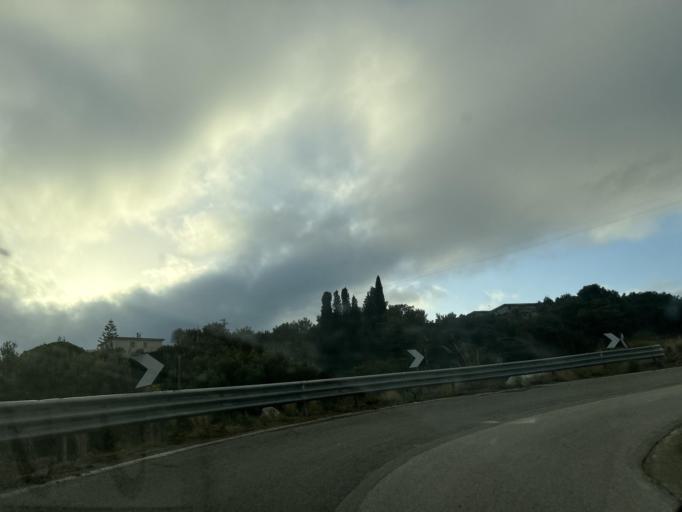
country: IT
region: Calabria
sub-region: Provincia di Catanzaro
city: Squillace Lido
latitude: 38.7590
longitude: 16.5616
